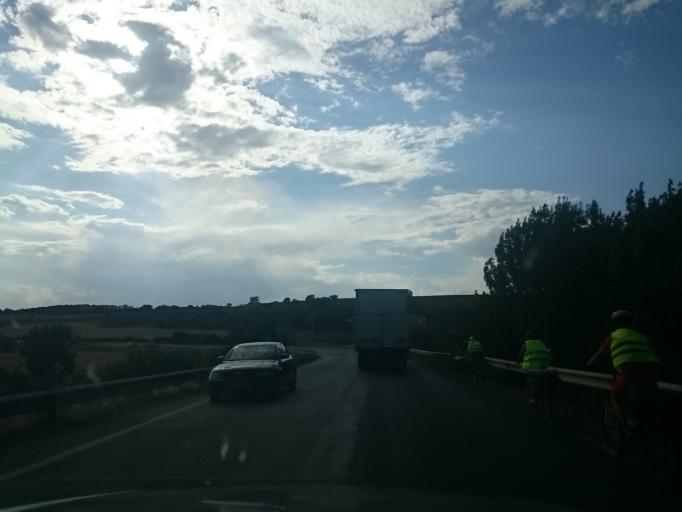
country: ES
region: Castille and Leon
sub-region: Provincia de Burgos
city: Belorado
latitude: 42.4183
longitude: -3.2026
